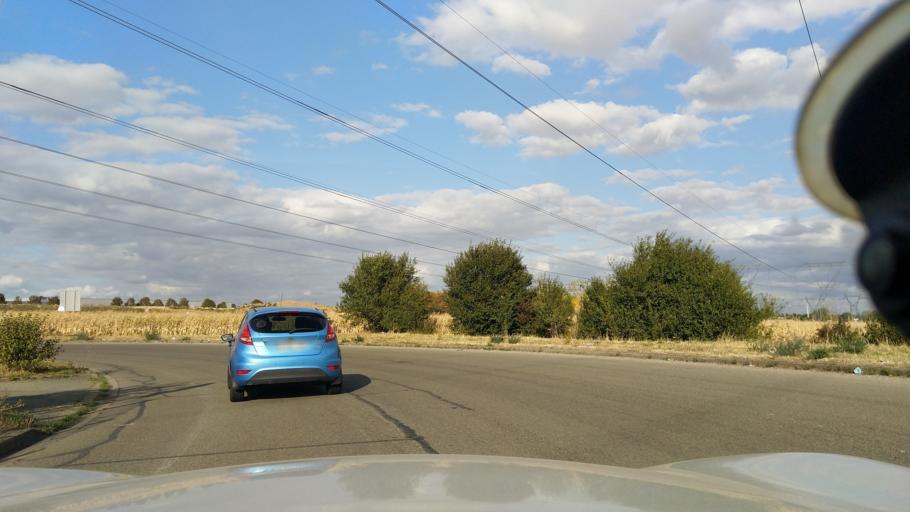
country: FR
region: Ile-de-France
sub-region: Departement de Seine-Saint-Denis
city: Villepinte
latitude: 48.9834
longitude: 2.5258
